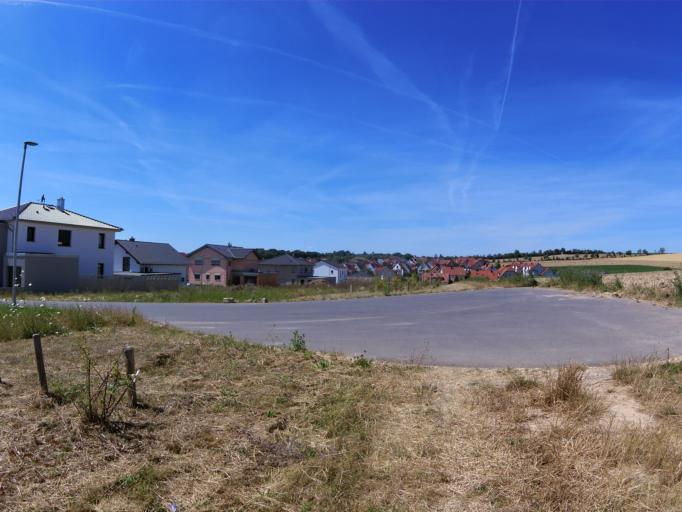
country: DE
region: Bavaria
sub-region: Regierungsbezirk Unterfranken
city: Hettstadt
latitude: 49.8033
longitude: 9.8285
